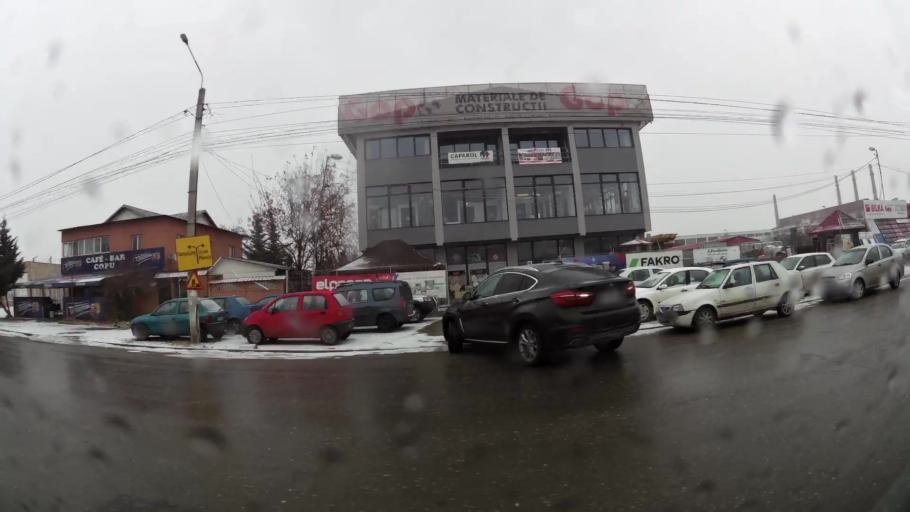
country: RO
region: Dambovita
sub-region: Municipiul Targoviste
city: Targoviste
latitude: 44.9276
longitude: 25.4321
